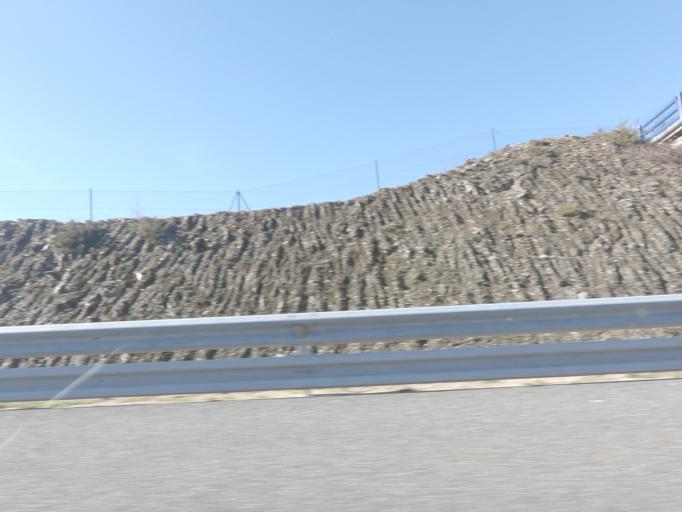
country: ES
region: Galicia
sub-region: Provincia de Pontevedra
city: Dozon
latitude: 42.5714
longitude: -8.0606
